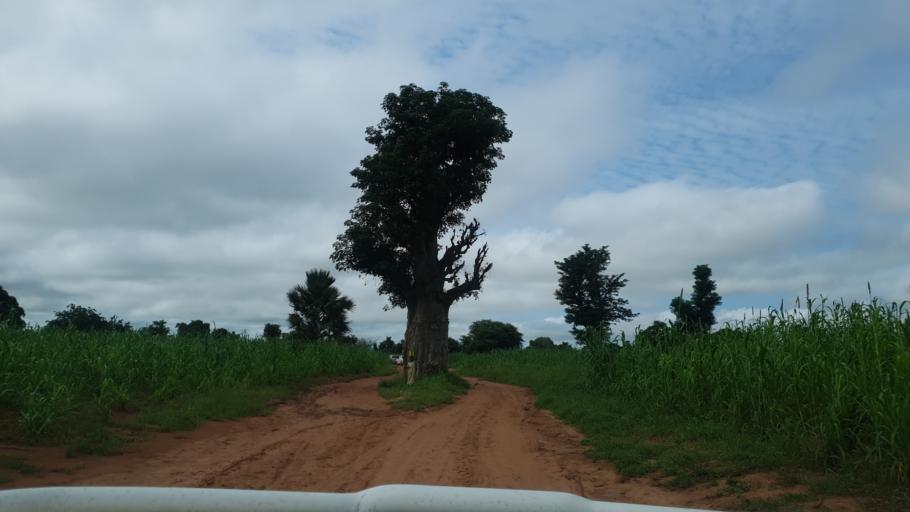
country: ML
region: Segou
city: Baroueli
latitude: 13.5030
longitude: -6.8982
